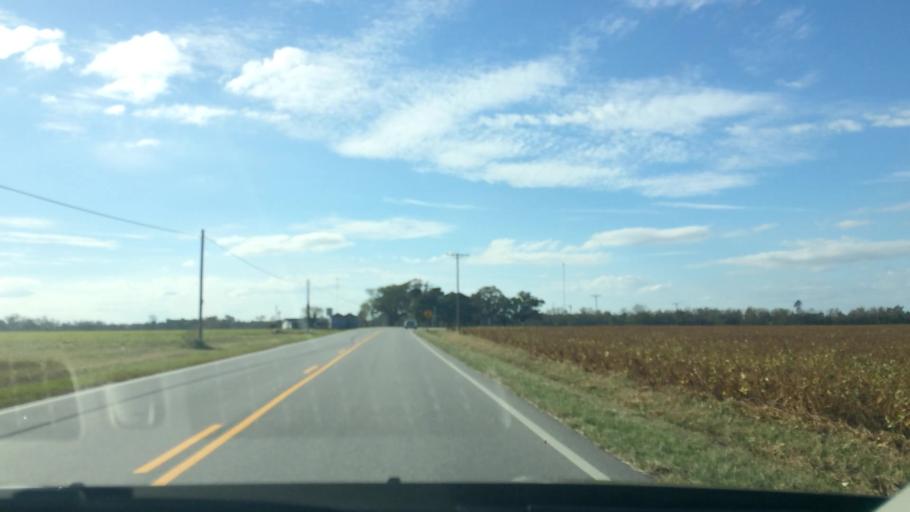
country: US
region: North Carolina
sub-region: Greene County
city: Maury
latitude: 35.4807
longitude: -77.6339
